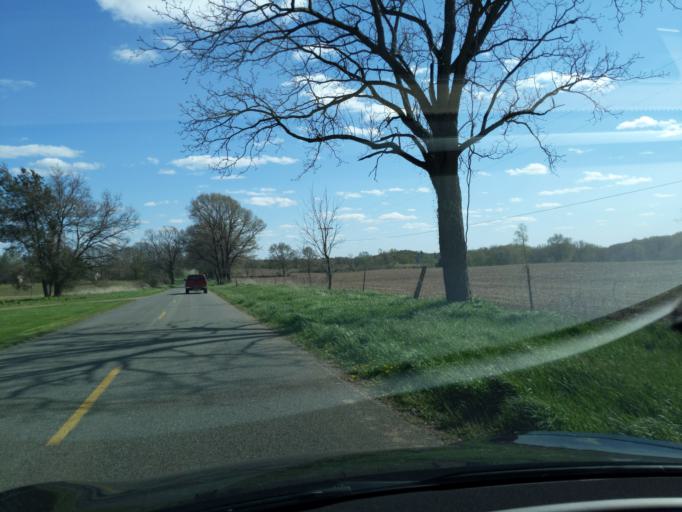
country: US
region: Michigan
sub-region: Ingham County
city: Leslie
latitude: 42.3522
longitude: -84.5318
